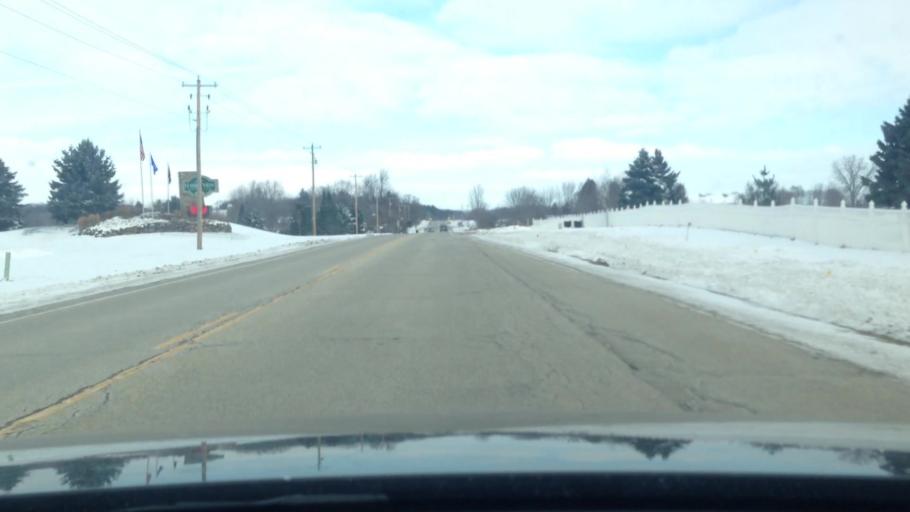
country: US
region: Wisconsin
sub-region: Walworth County
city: Lake Geneva
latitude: 42.6214
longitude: -88.4137
